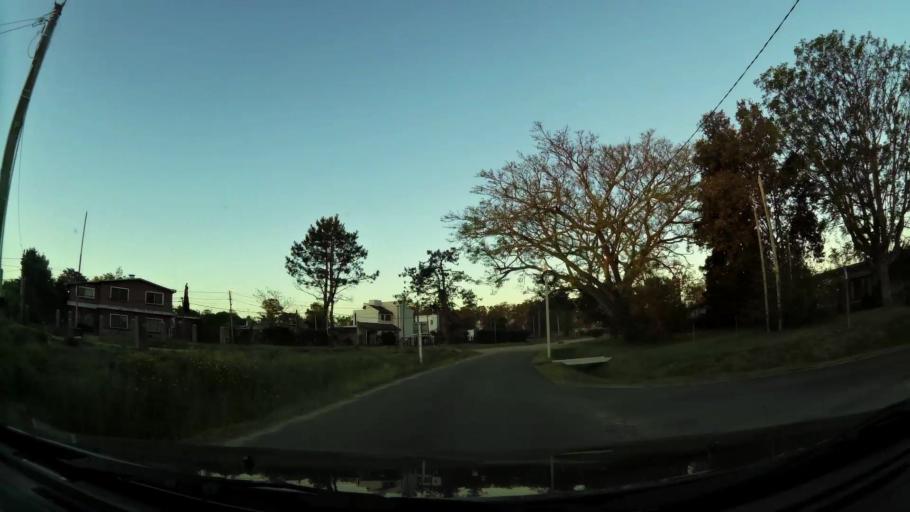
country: UY
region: Canelones
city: Barra de Carrasco
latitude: -34.8318
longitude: -55.9623
